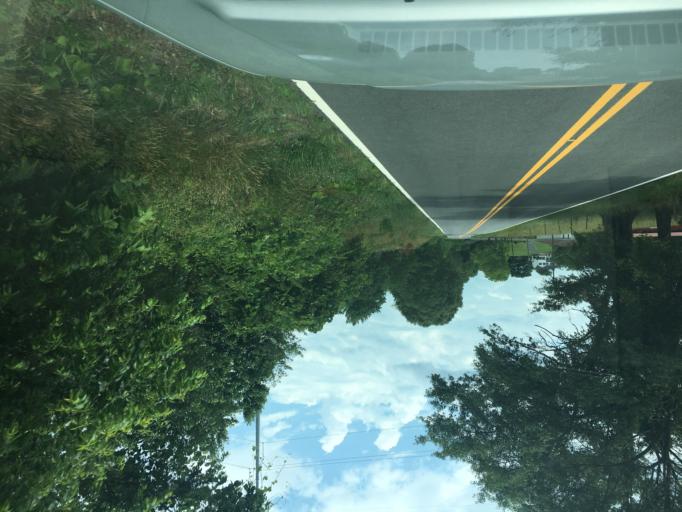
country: US
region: South Carolina
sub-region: Spartanburg County
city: Duncan
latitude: 34.8766
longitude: -82.1839
